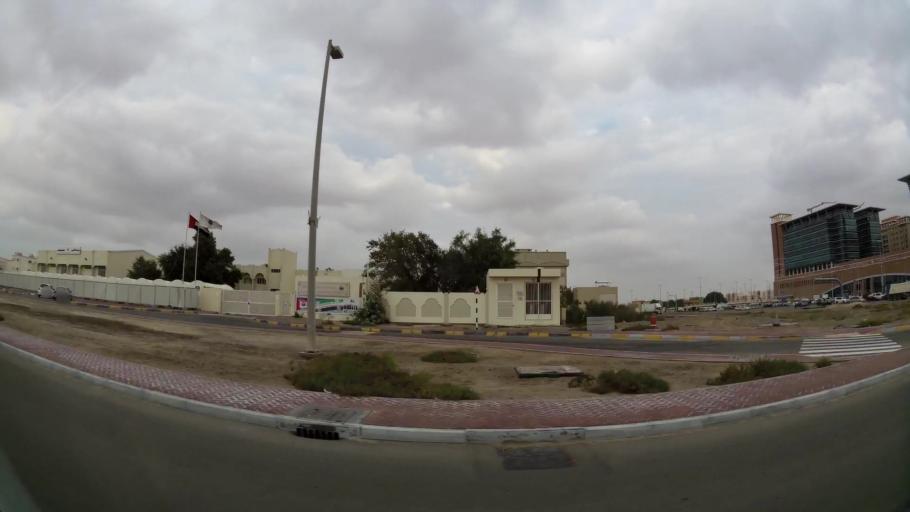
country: AE
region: Abu Dhabi
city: Abu Dhabi
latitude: 24.3751
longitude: 54.5362
